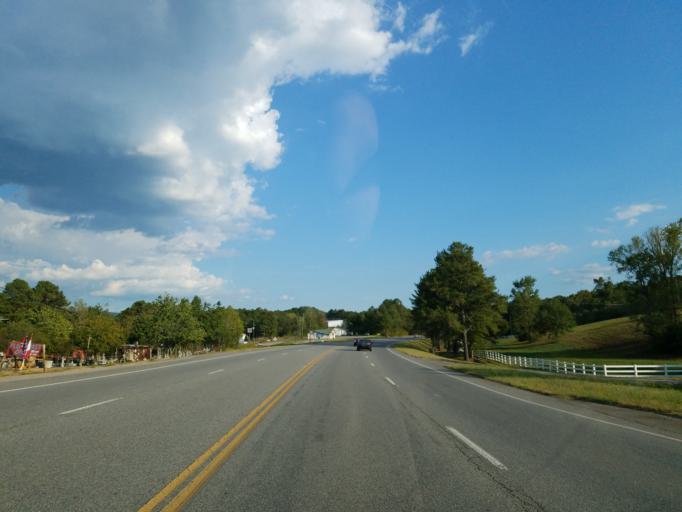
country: US
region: Georgia
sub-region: Murray County
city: Chatsworth
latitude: 34.7333
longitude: -84.7543
